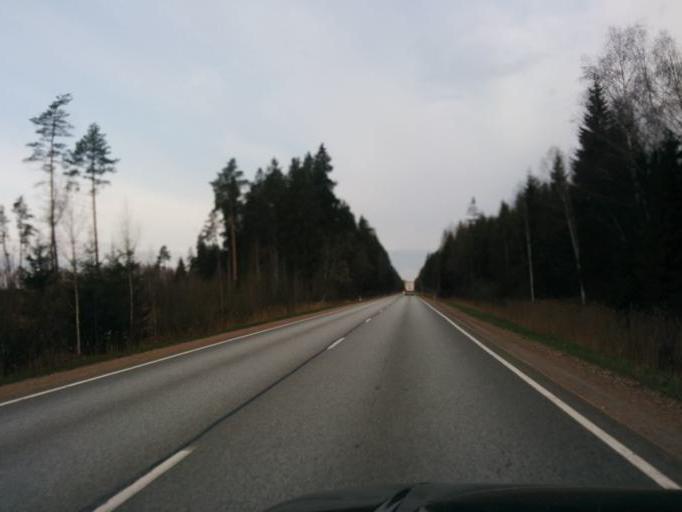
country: LV
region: Kekava
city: Balozi
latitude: 56.8134
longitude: 24.1483
